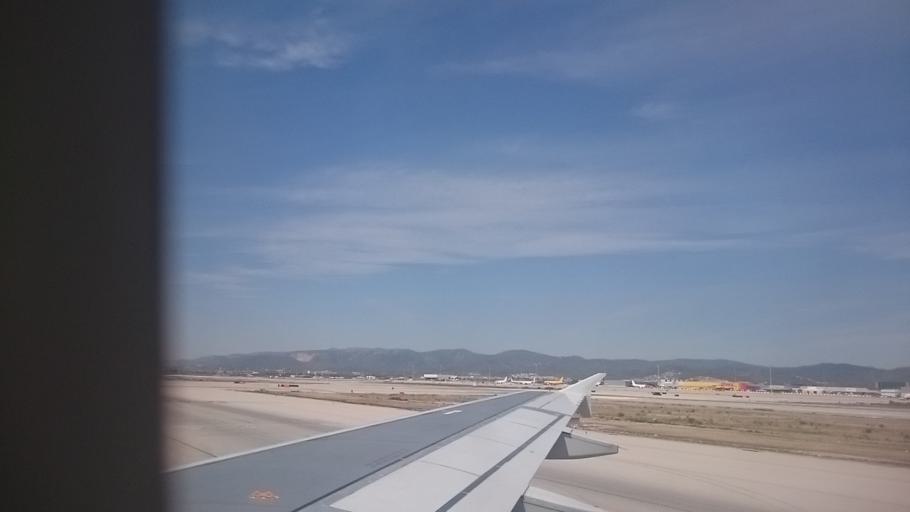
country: ES
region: Catalonia
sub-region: Provincia de Barcelona
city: El Prat de Llobregat
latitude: 41.2939
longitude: 2.0753
